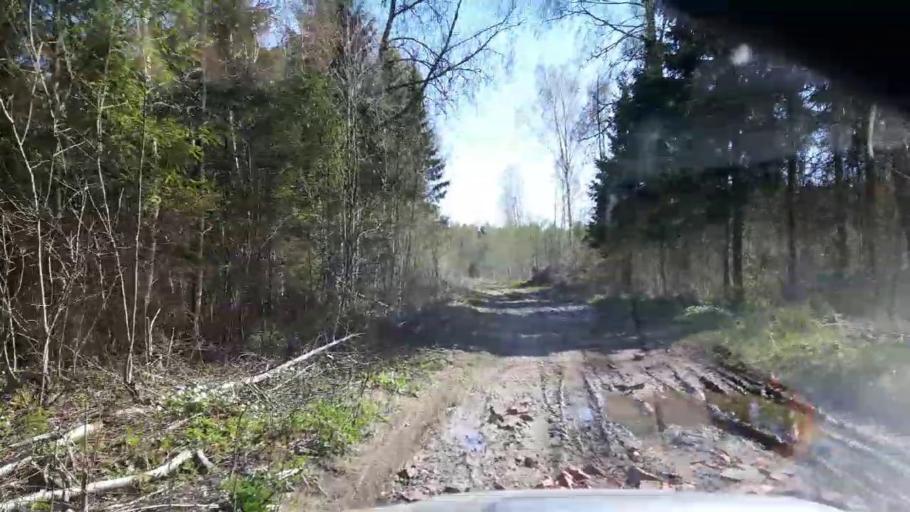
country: EE
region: Paernumaa
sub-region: Tootsi vald
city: Tootsi
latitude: 58.5437
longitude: 24.8024
